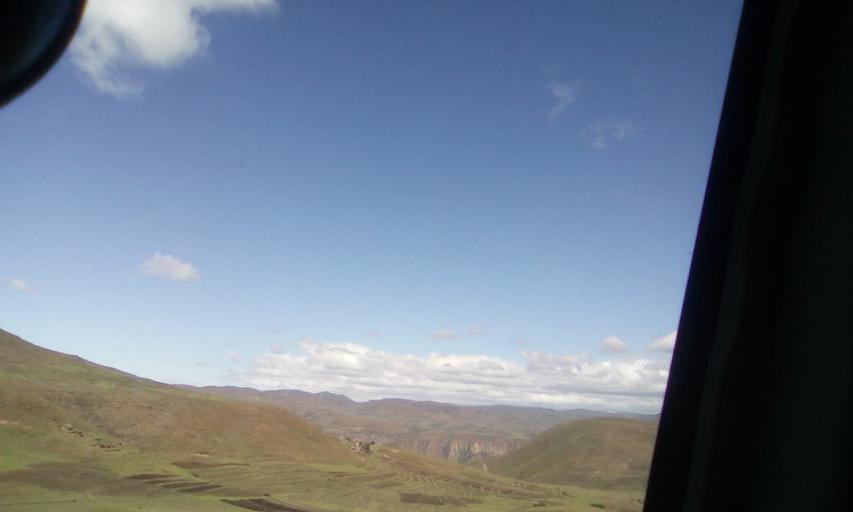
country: LS
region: Maseru
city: Nako
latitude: -29.8881
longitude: 28.1074
